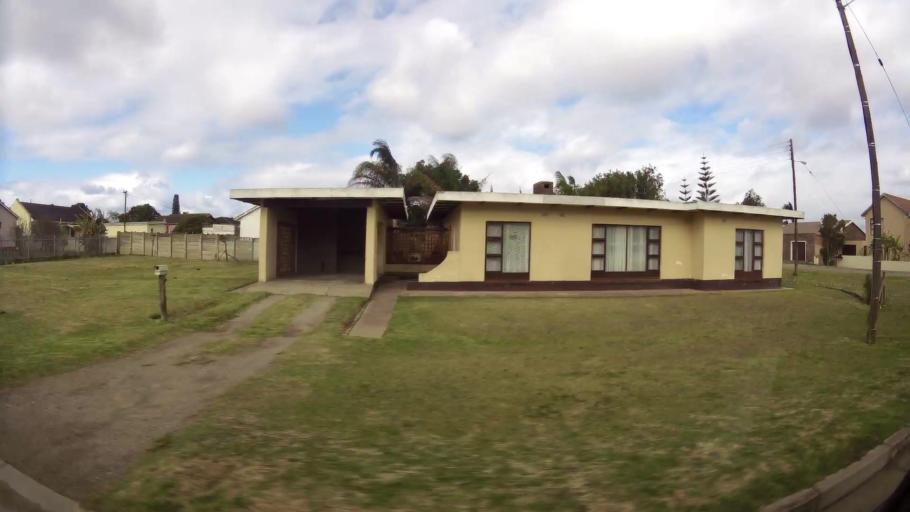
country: ZA
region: Western Cape
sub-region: Eden District Municipality
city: George
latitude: -34.0023
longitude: 22.4431
